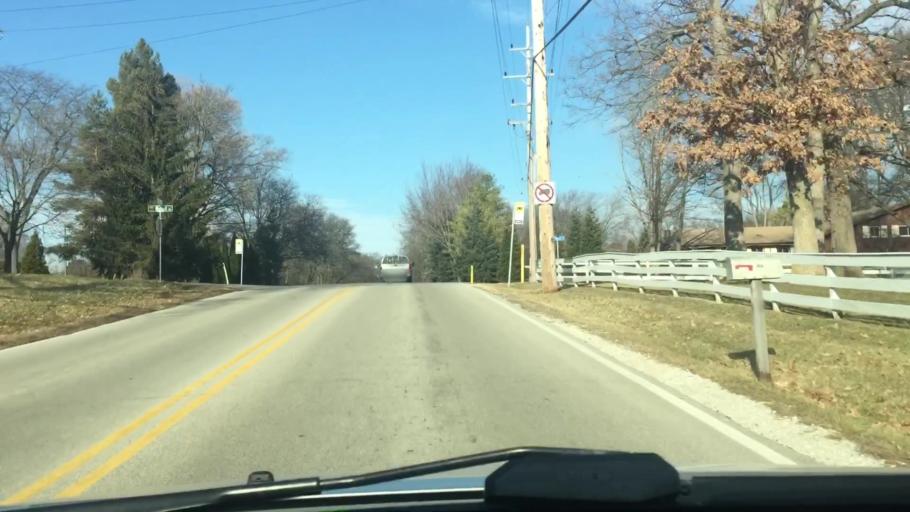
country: US
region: Wisconsin
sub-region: Waukesha County
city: Elm Grove
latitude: 43.0524
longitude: -88.0668
